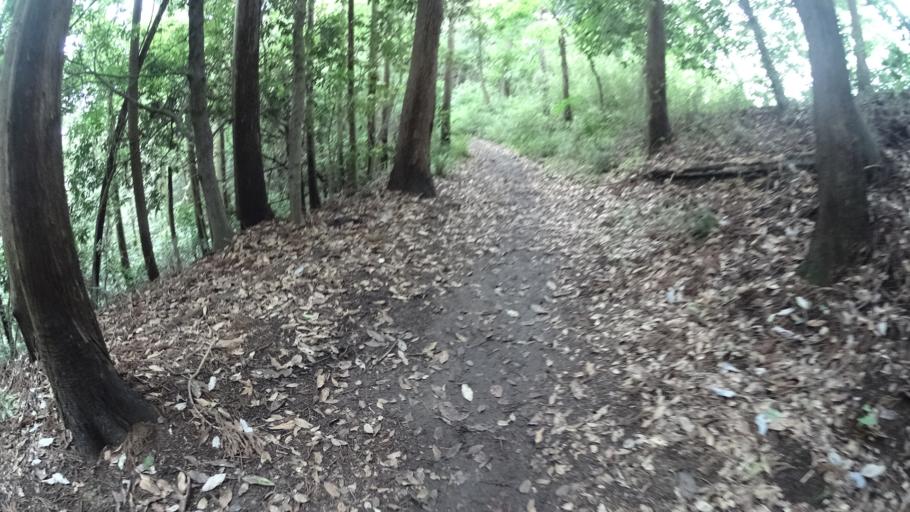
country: JP
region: Kanagawa
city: Kamakura
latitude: 35.3359
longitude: 139.5836
